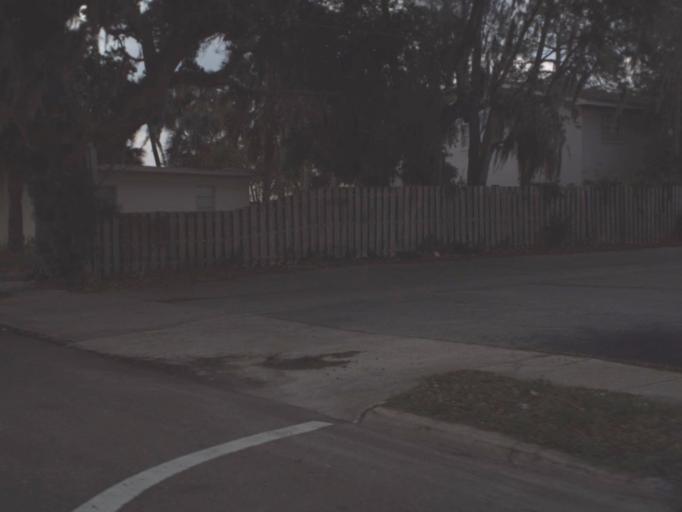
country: US
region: Florida
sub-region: Lake County
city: Eustis
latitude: 28.8558
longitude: -81.6836
